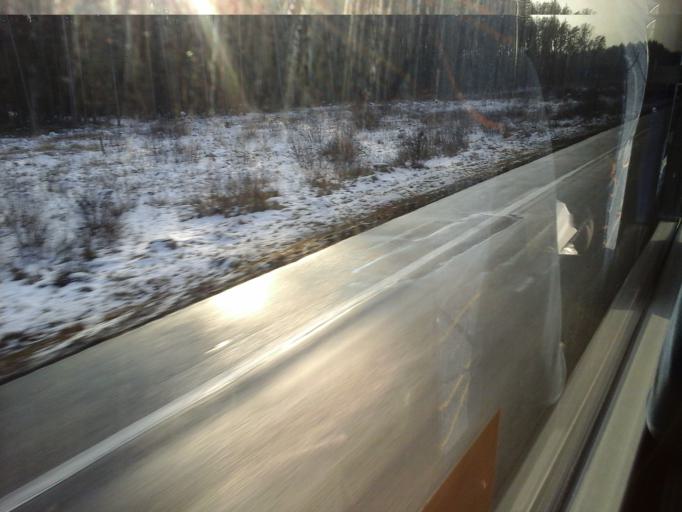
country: PL
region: Warmian-Masurian Voivodeship
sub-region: Powiat olsztynski
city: Olsztynek
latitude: 53.5853
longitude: 20.1963
